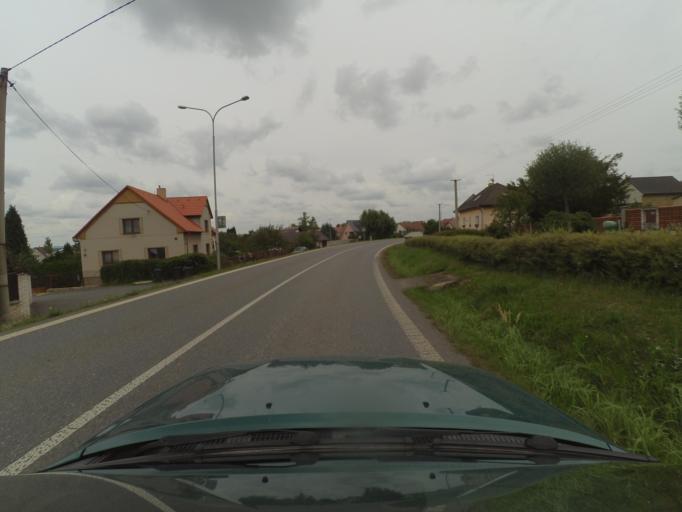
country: CZ
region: Central Bohemia
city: Pavlikov
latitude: 50.0764
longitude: 13.7035
